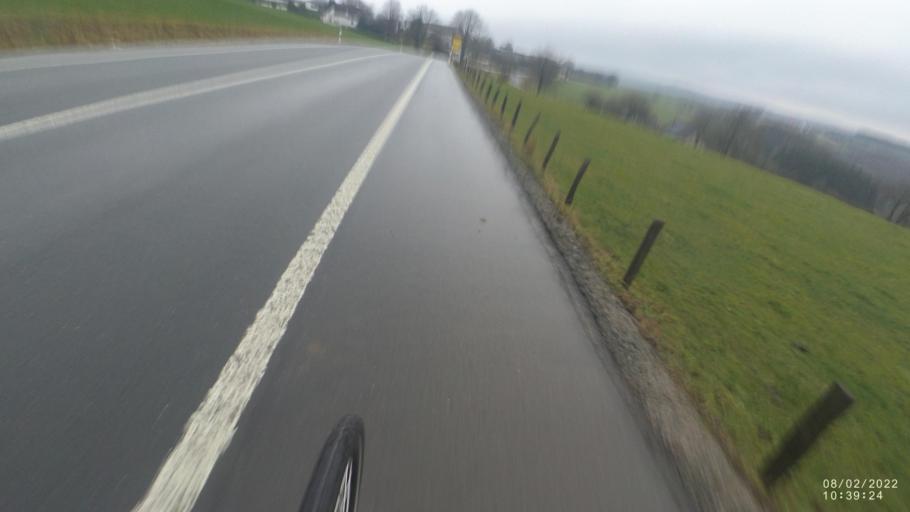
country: DE
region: North Rhine-Westphalia
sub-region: Regierungsbezirk Arnsberg
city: Schalksmuhle
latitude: 51.2600
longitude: 7.5695
